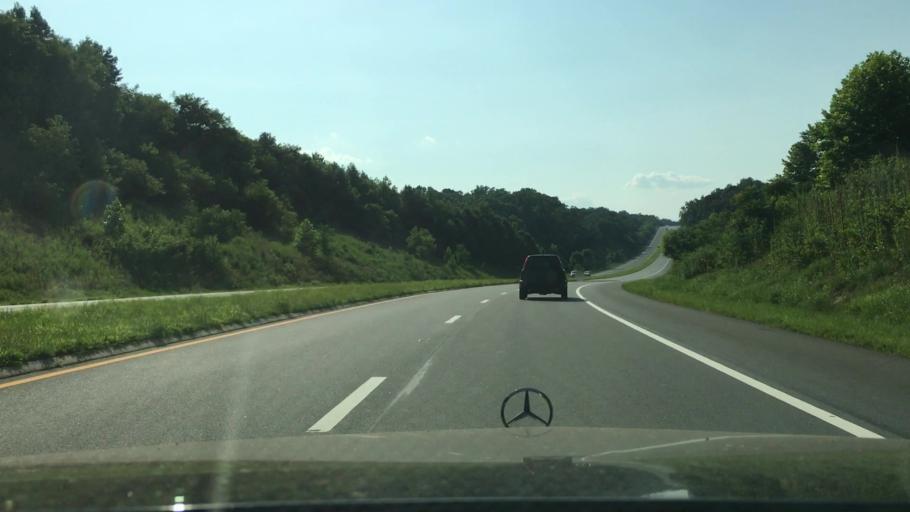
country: US
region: Virginia
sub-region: Amherst County
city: Madison Heights
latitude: 37.4145
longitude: -79.1086
